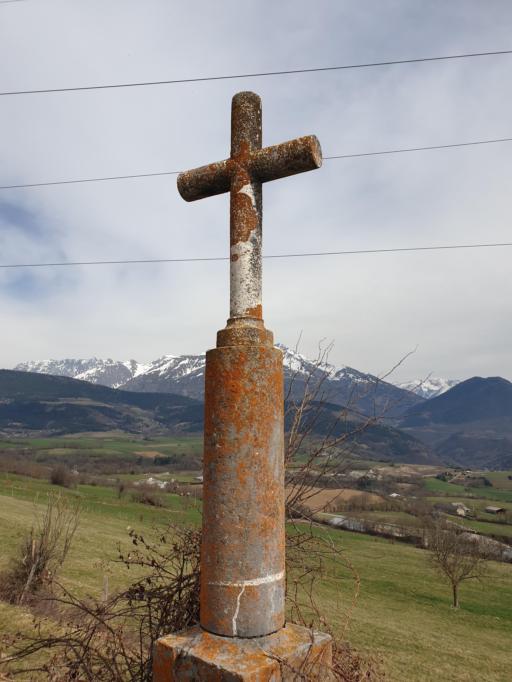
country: FR
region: Rhone-Alpes
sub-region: Departement de l'Isere
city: La Mure
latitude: 44.9159
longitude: 5.7954
